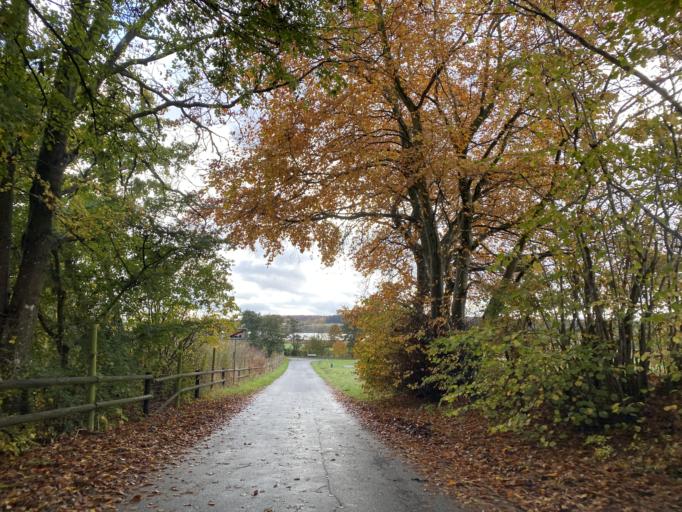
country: DK
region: Central Jutland
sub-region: Skanderborg Kommune
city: Skovby
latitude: 56.2227
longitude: 9.9574
